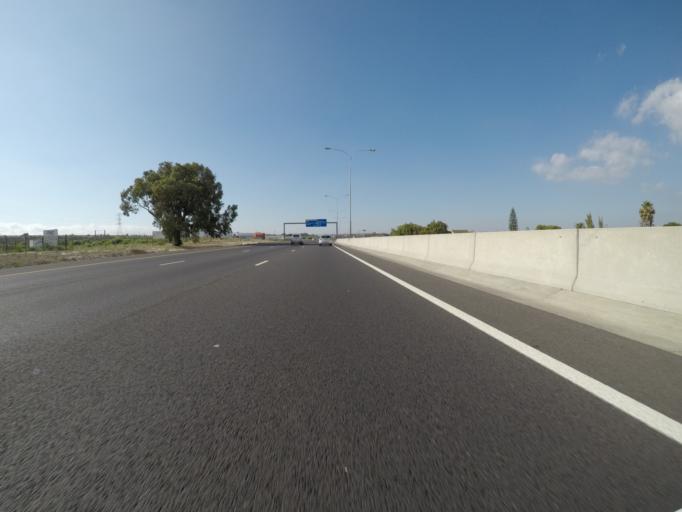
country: ZA
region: Western Cape
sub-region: City of Cape Town
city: Kraaifontein
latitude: -33.9245
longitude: 18.6634
